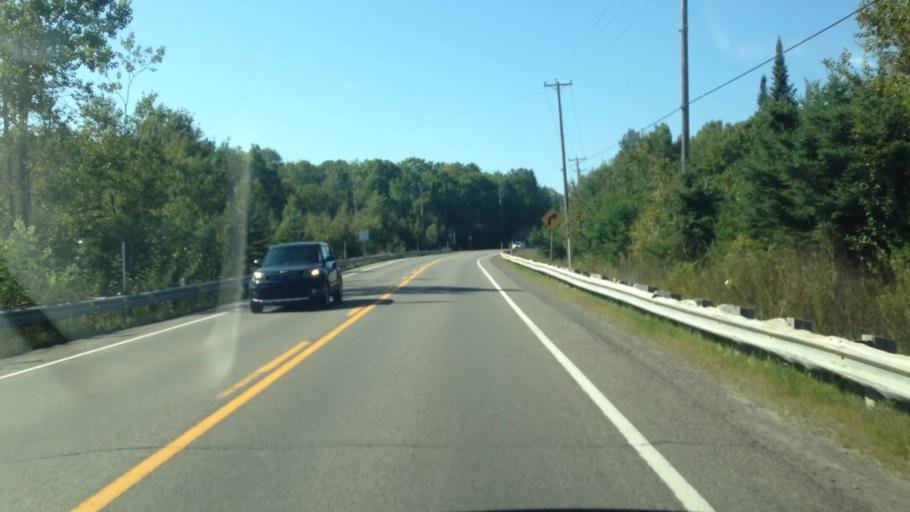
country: CA
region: Quebec
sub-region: Laurentides
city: Prevost
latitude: 45.9045
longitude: -74.0015
